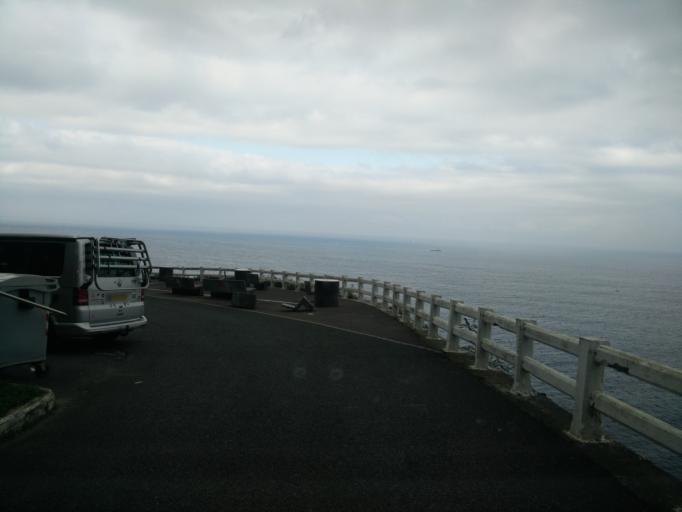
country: ES
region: Basque Country
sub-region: Provincia de Guipuzcoa
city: Deba
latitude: 43.3009
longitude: -2.3402
